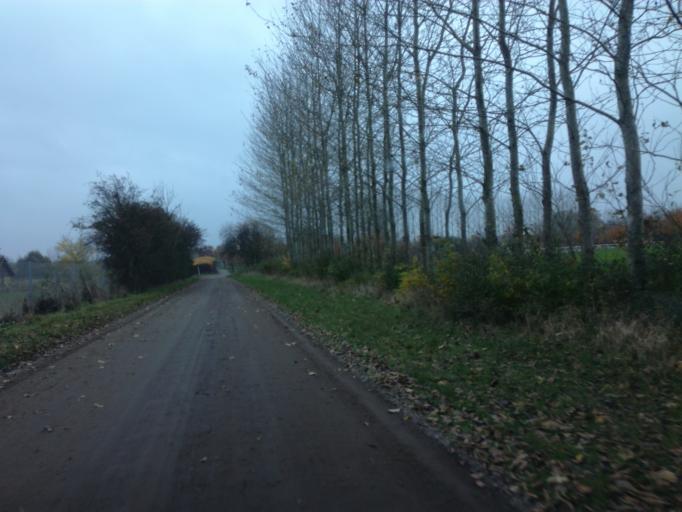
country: DK
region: South Denmark
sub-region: Fredericia Kommune
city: Fredericia
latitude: 55.5804
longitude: 9.7205
